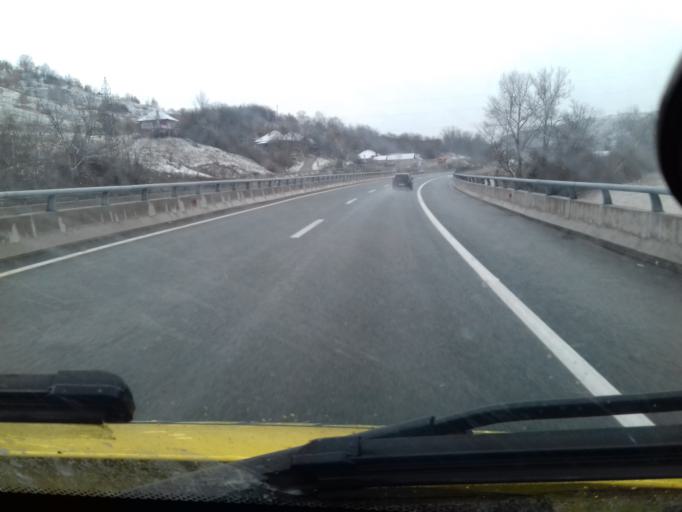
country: BA
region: Federation of Bosnia and Herzegovina
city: Kakanj
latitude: 44.1341
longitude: 18.0825
